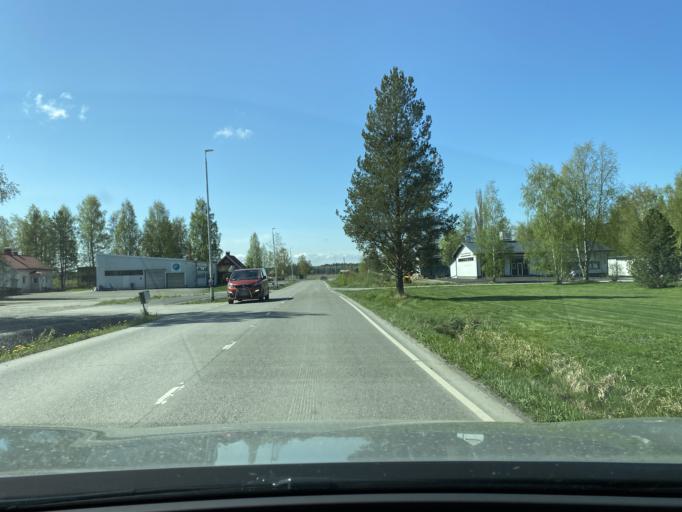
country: FI
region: Pirkanmaa
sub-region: Lounais-Pirkanmaa
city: Vammala
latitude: 61.3304
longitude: 22.9136
